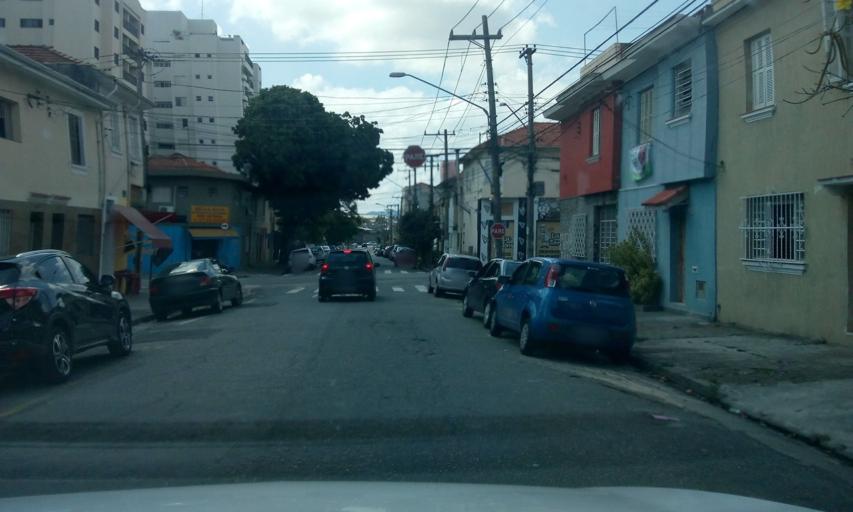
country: BR
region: Sao Paulo
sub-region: Sao Paulo
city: Sao Paulo
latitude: -23.5231
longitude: -46.7104
